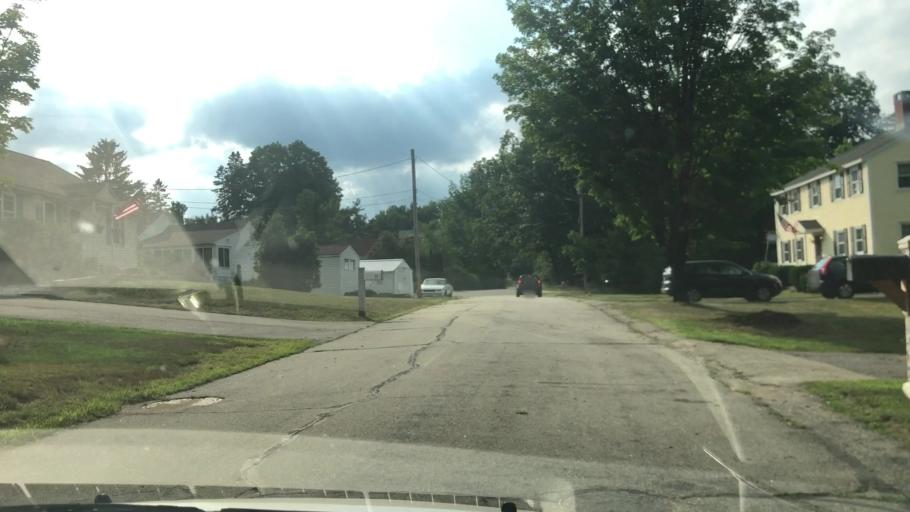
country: US
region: New Hampshire
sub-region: Hillsborough County
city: Milford
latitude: 42.8310
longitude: -71.6344
